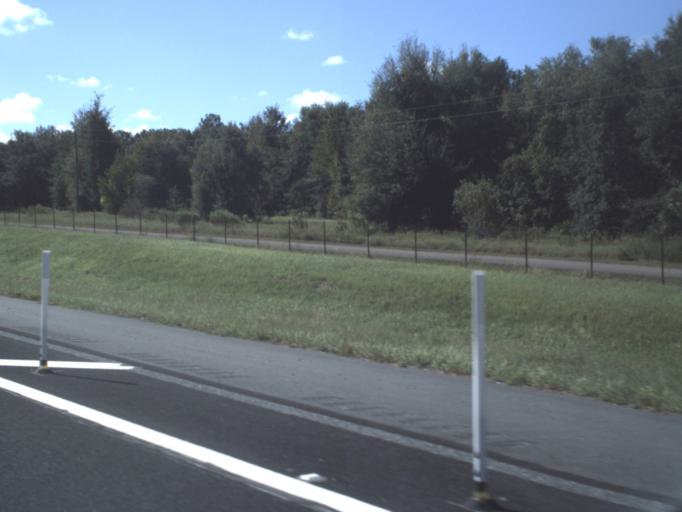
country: US
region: Florida
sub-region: Citrus County
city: Sugarmill Woods
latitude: 28.6668
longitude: -82.4940
